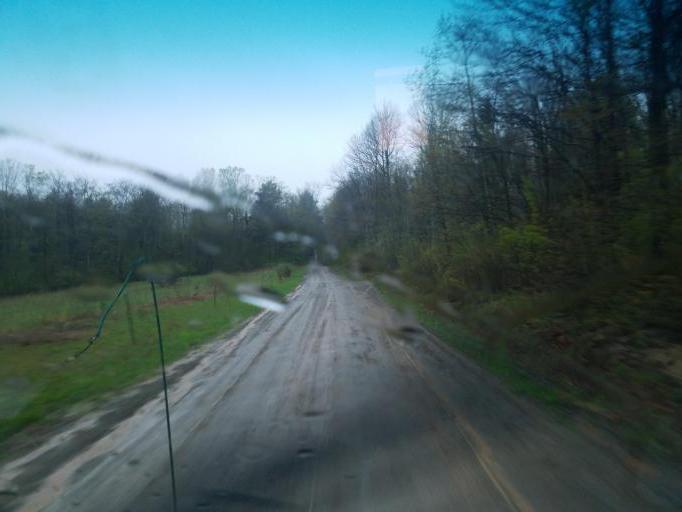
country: US
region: Pennsylvania
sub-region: Tioga County
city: Westfield
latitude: 41.9316
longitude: -77.6988
